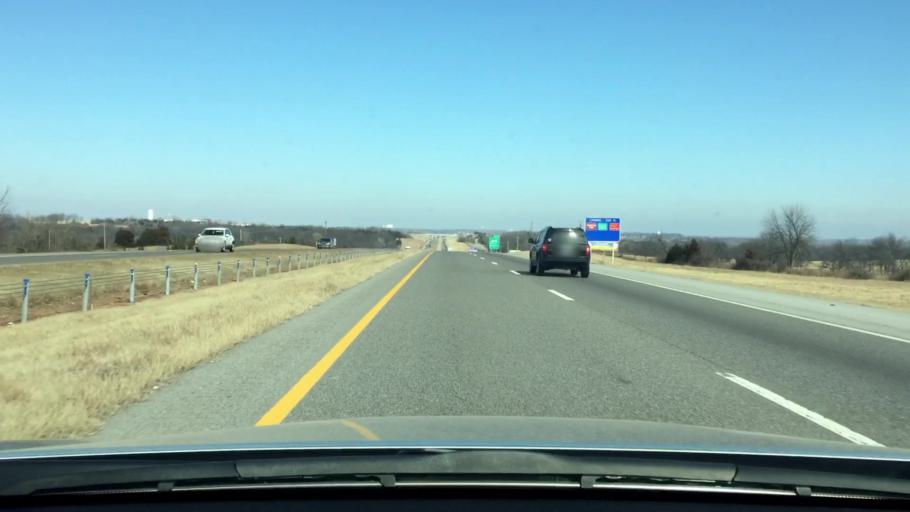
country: US
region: Oklahoma
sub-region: McClain County
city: Purcell
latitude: 34.9626
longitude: -97.3695
